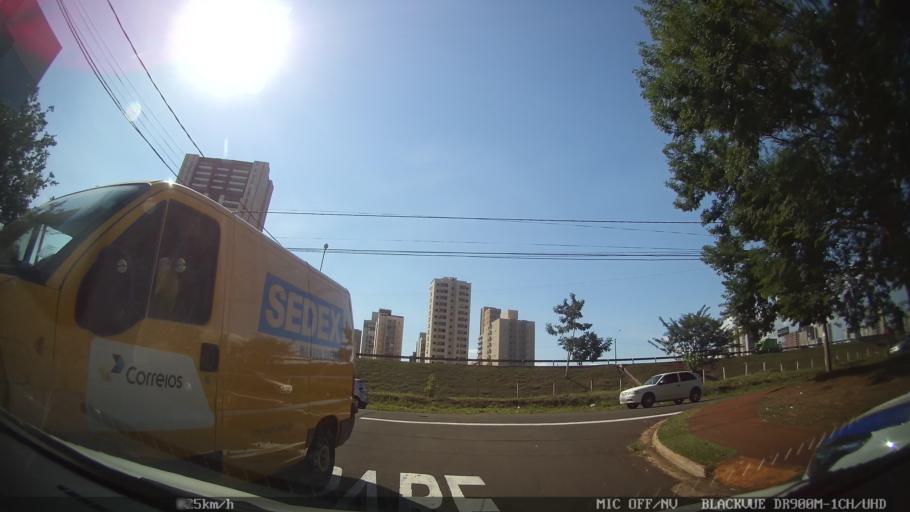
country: BR
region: Sao Paulo
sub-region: Ribeirao Preto
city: Ribeirao Preto
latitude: -21.2198
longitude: -47.8289
